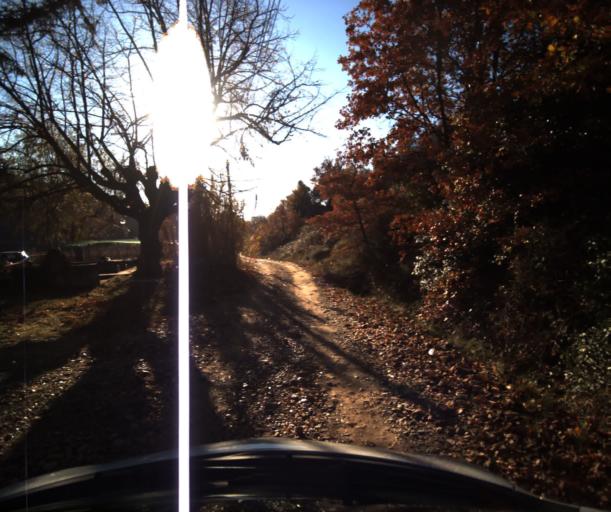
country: FR
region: Provence-Alpes-Cote d'Azur
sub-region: Departement du Vaucluse
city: Pertuis
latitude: 43.7185
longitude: 5.4944
